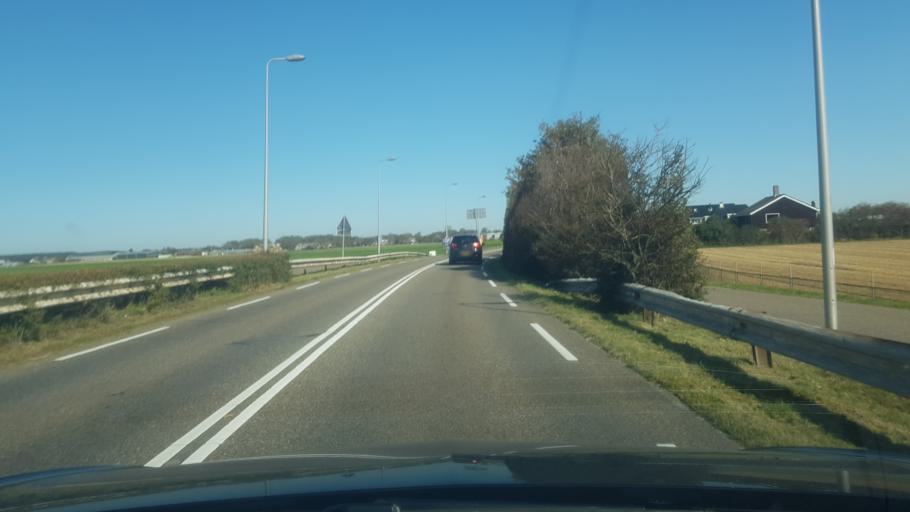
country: NL
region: South Holland
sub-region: Gemeente Noordwijkerhout
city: Noordwijkerhout
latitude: 52.2523
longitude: 4.4771
